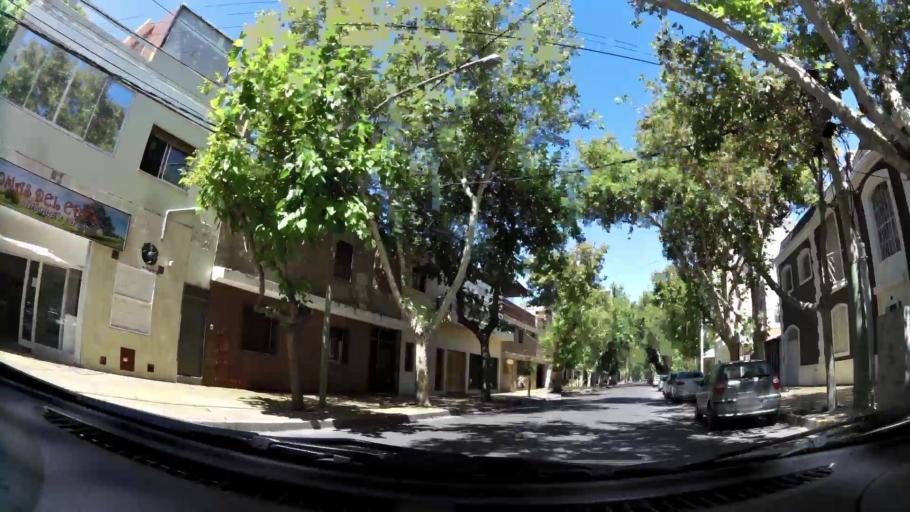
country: AR
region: San Juan
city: San Juan
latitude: -31.5348
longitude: -68.5162
